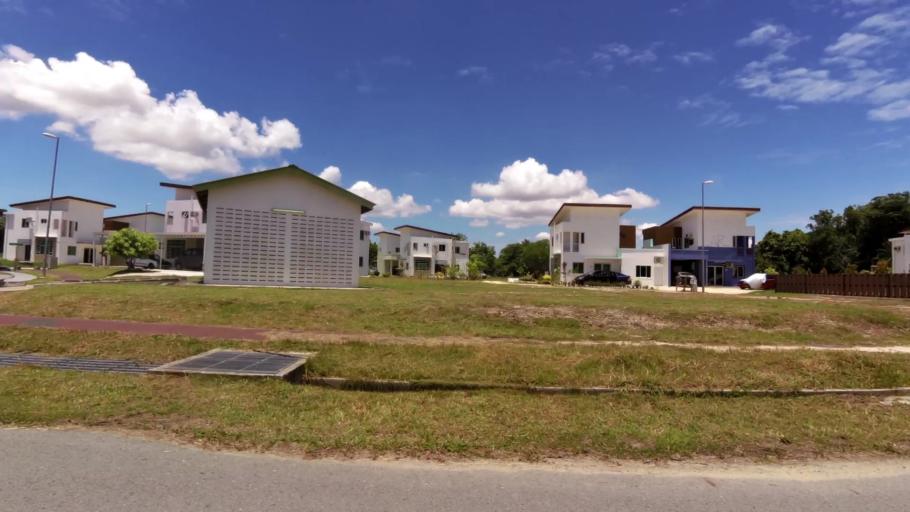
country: BN
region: Brunei and Muara
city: Bandar Seri Begawan
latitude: 5.0062
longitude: 115.0048
